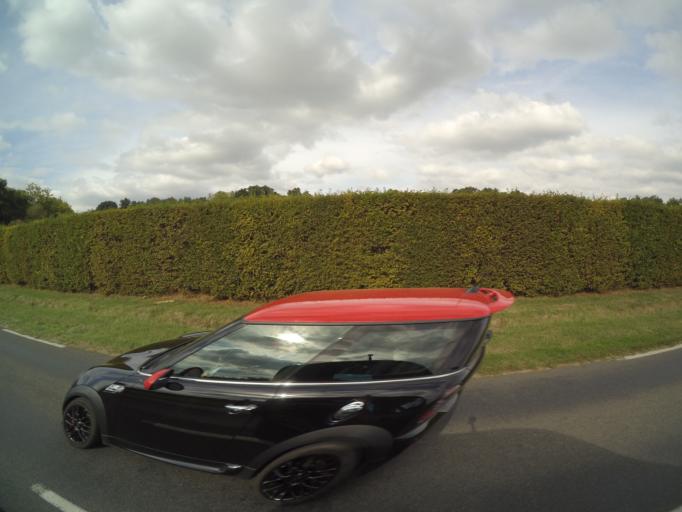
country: FR
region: Centre
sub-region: Departement d'Indre-et-Loire
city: Vernou-sur-Brenne
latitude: 47.4114
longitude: 0.8334
